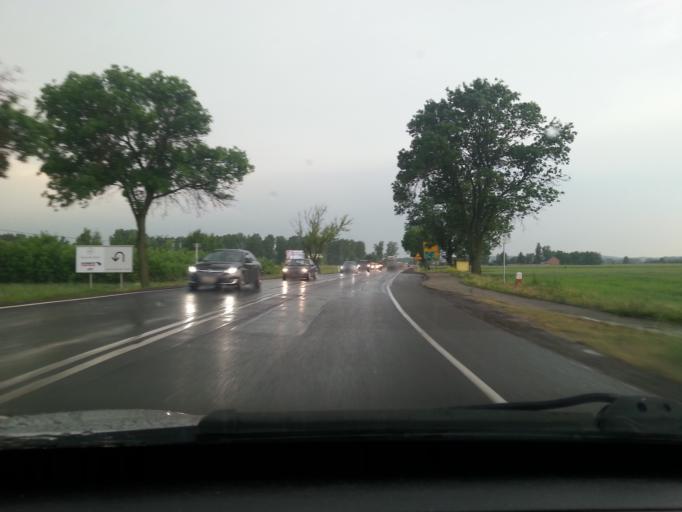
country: PL
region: Lodz Voivodeship
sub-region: Powiat zgierski
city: Strykow
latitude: 51.8813
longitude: 19.5822
